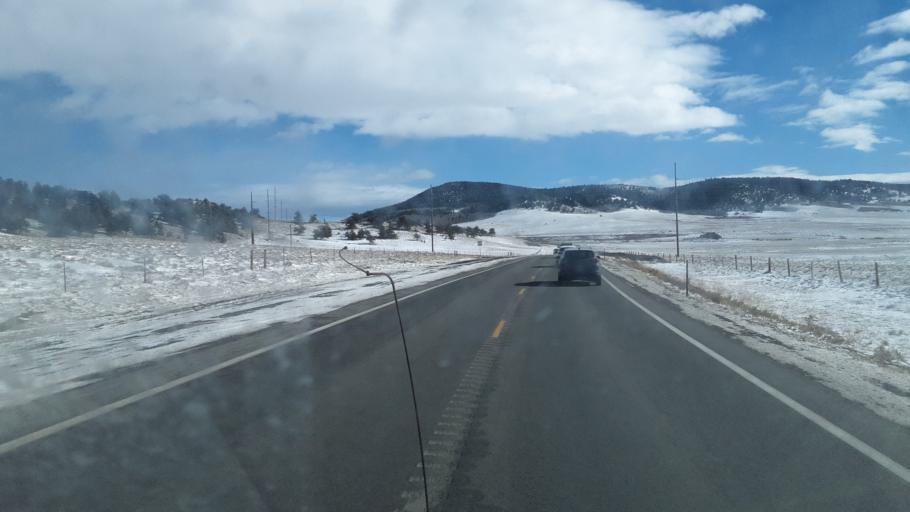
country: US
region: Colorado
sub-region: Park County
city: Fairplay
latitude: 39.2764
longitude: -105.9440
